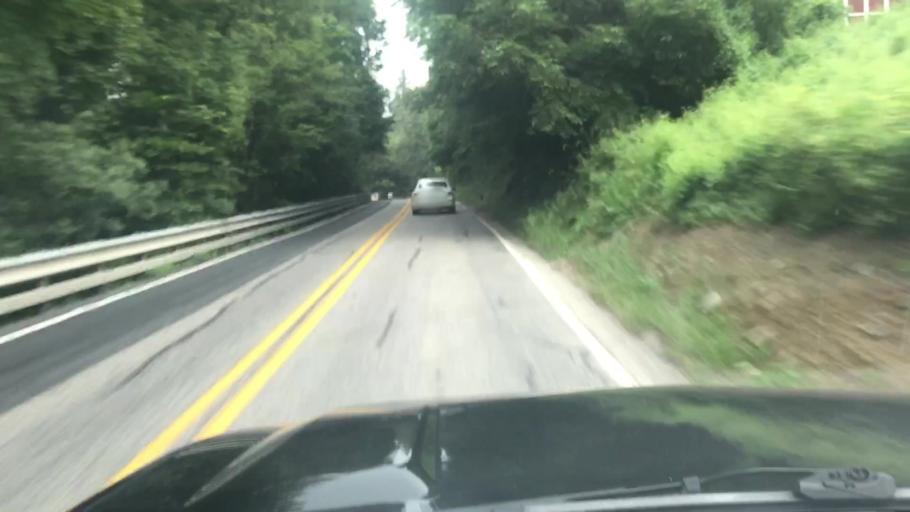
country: US
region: Pennsylvania
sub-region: Cumberland County
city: Shiremanstown
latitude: 40.2550
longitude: -76.9756
